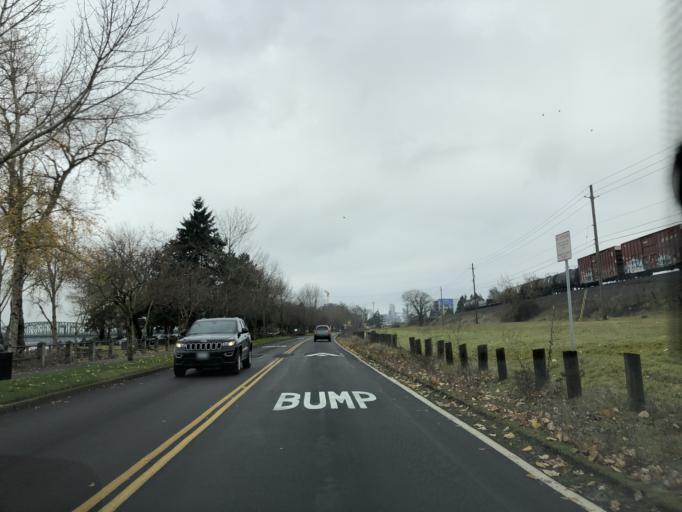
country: US
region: Washington
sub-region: Clark County
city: Vancouver
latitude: 45.6198
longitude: -122.6667
